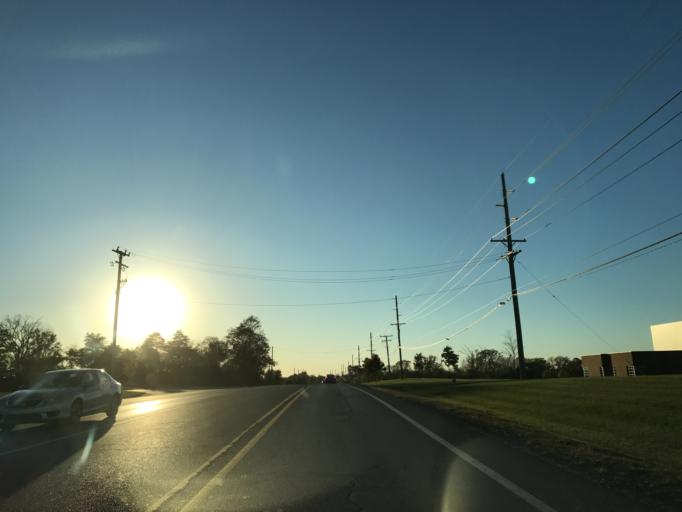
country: US
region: Michigan
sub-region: Oakland County
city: Wixom
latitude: 42.4639
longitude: -83.5638
